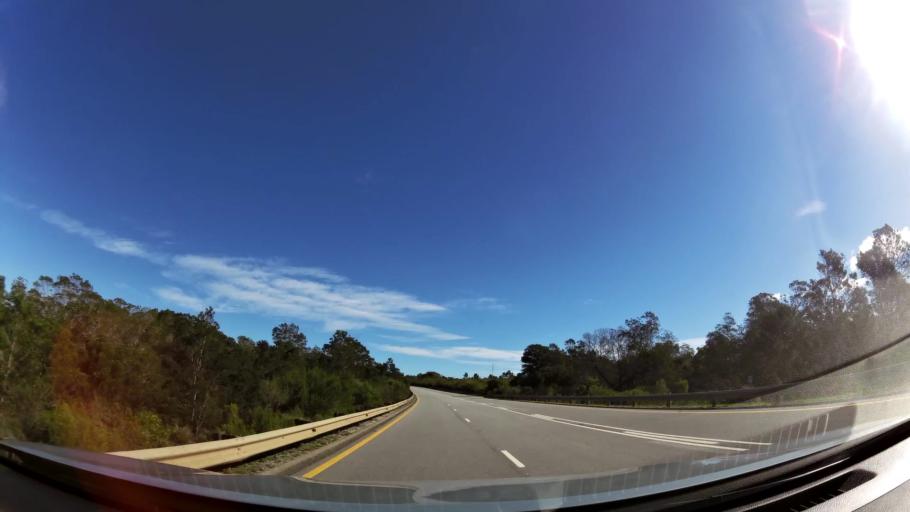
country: ZA
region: Eastern Cape
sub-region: Cacadu District Municipality
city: Kruisfontein
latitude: -34.0165
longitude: 24.6259
